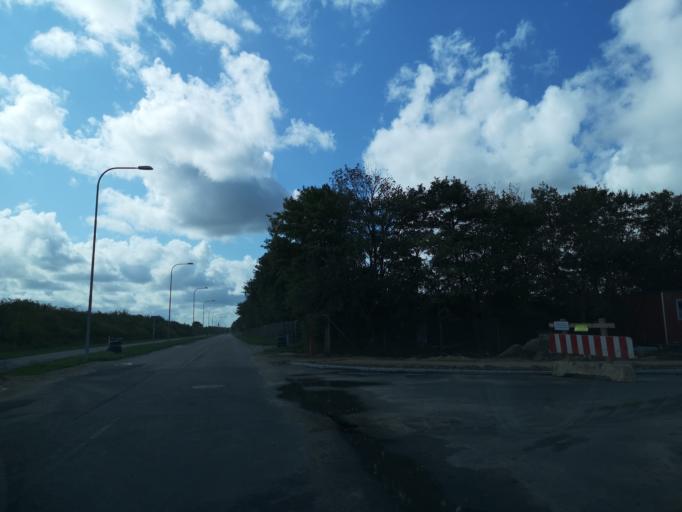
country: DK
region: Central Jutland
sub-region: Holstebro Kommune
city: Holstebro
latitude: 56.3911
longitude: 8.5812
